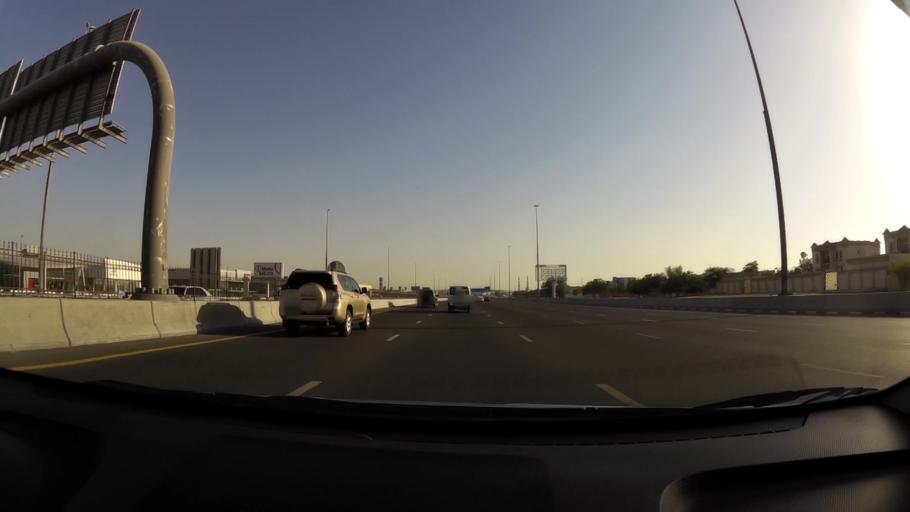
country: AE
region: Ash Shariqah
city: Sharjah
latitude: 25.3499
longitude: 55.4763
